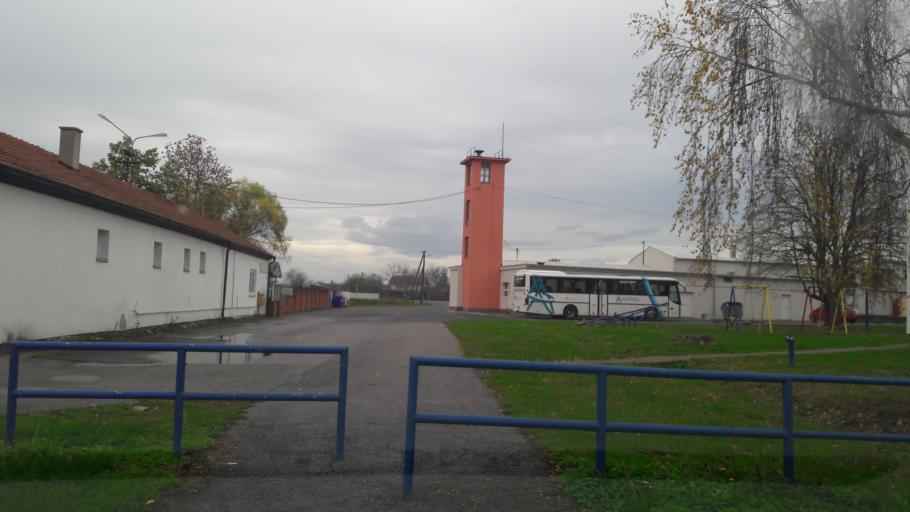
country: HR
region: Osjecko-Baranjska
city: Koska
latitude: 45.5438
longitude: 18.2859
